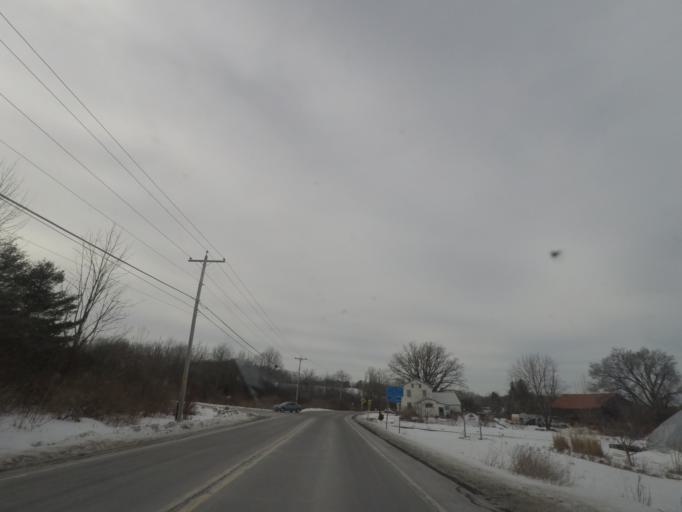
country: US
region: New York
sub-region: Albany County
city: Altamont
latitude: 42.6774
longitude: -74.0843
